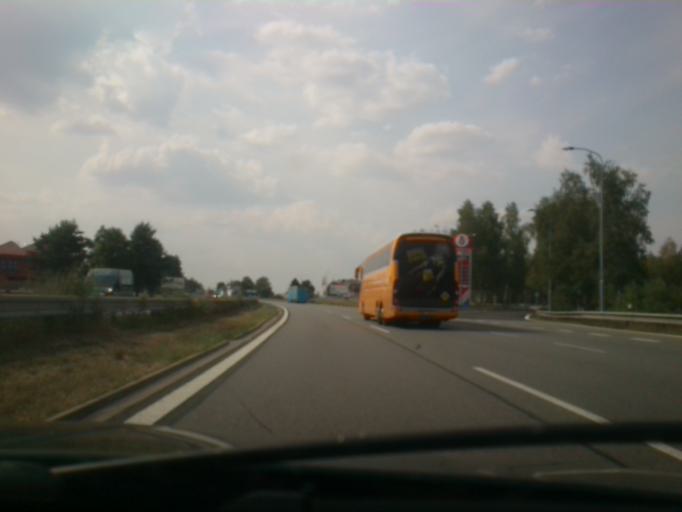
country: CZ
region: Central Bohemia
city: Trhovy Stepanov
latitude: 49.7517
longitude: 15.0246
